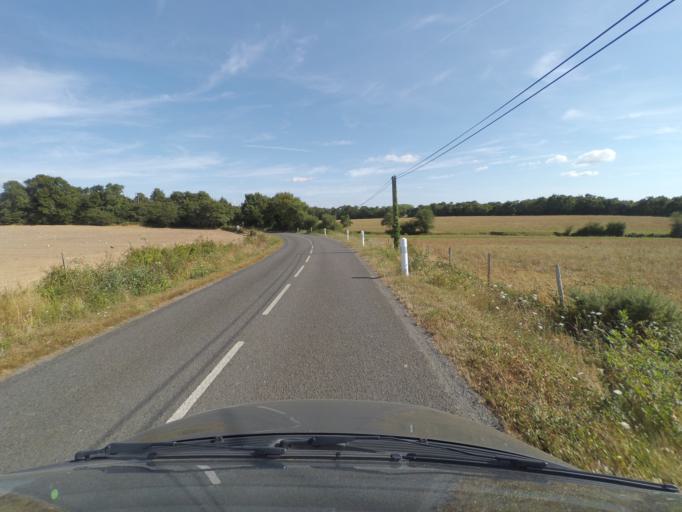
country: FR
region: Pays de la Loire
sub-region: Departement de la Loire-Atlantique
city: Les Sorinieres
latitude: 47.1162
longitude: -1.5223
